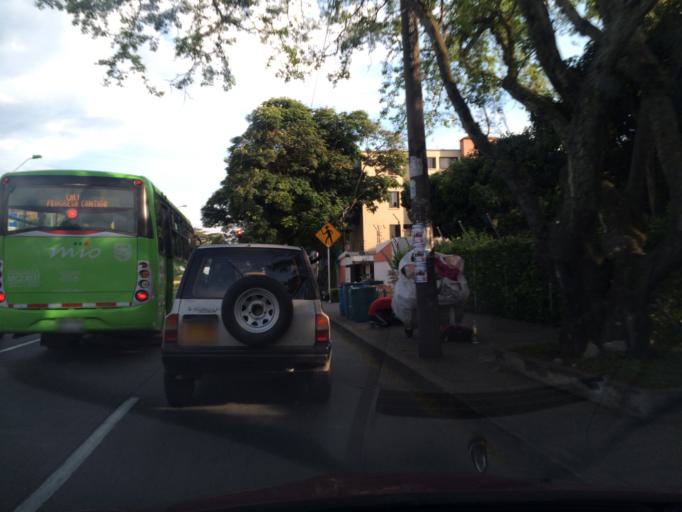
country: CO
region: Valle del Cauca
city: Cali
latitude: 3.3989
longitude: -76.5466
